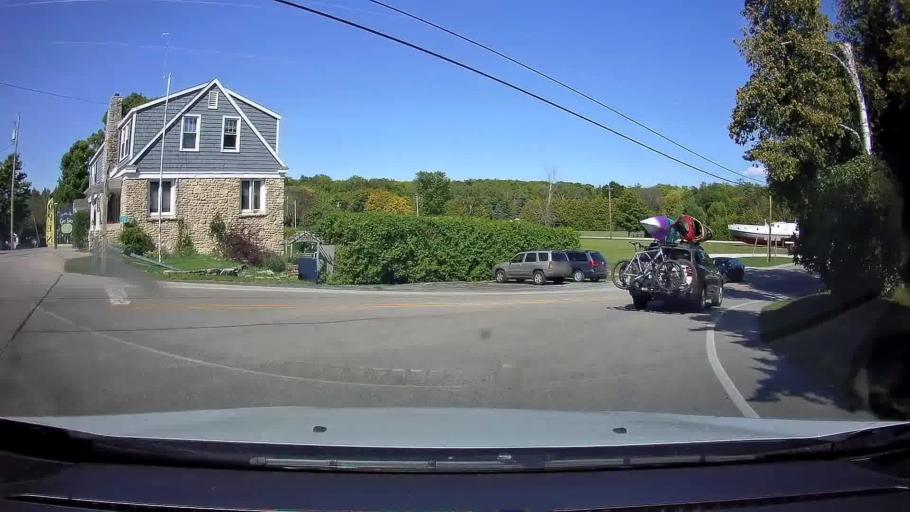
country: US
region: Michigan
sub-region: Delta County
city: Escanaba
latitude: 45.2904
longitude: -87.0217
